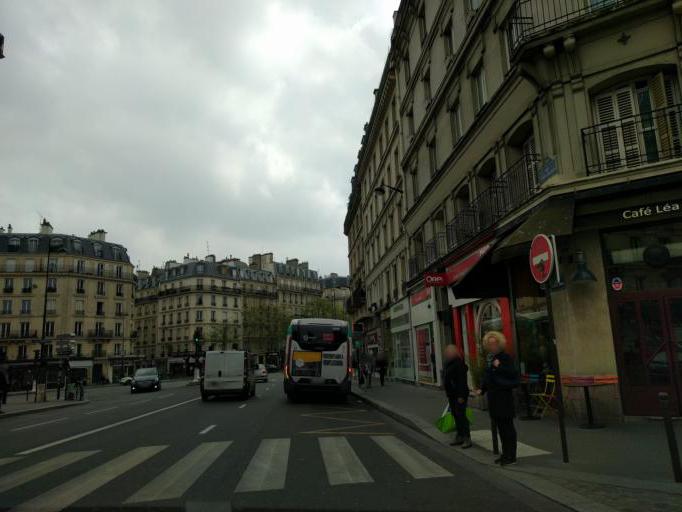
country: FR
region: Ile-de-France
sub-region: Paris
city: Paris
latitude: 48.8388
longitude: 2.3499
